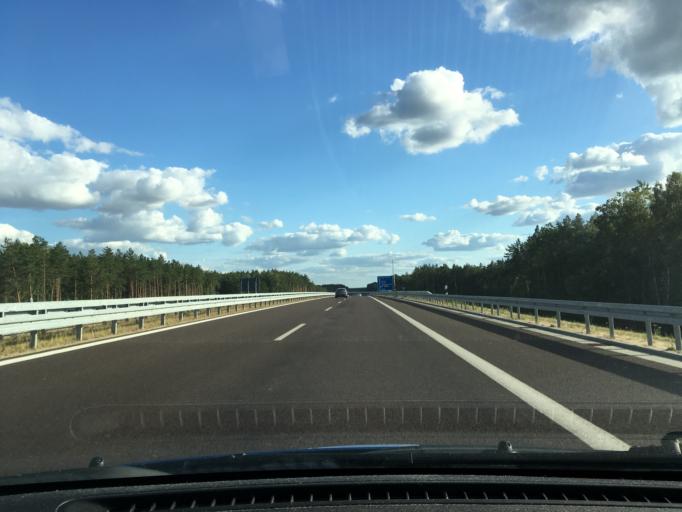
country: DE
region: Mecklenburg-Vorpommern
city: Ludwigslust
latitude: 53.3073
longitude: 11.5275
